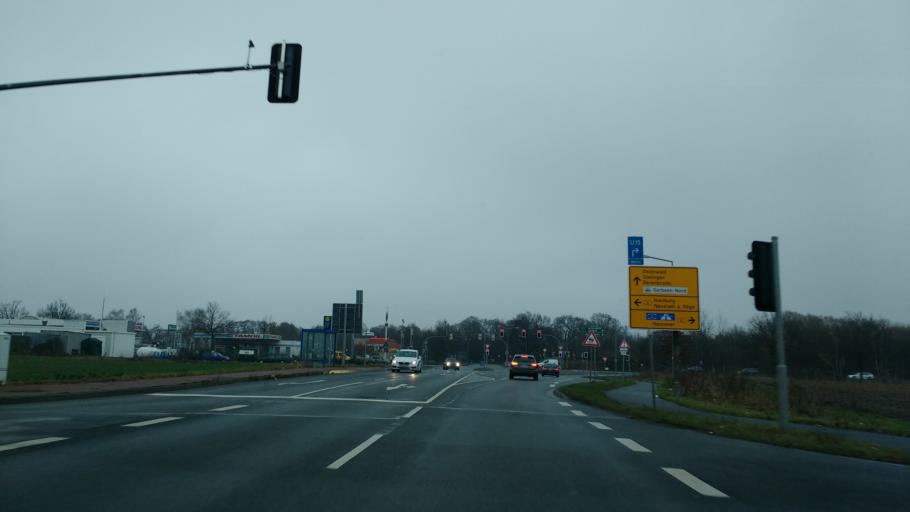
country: DE
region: Lower Saxony
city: Garbsen-Mitte
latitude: 52.4380
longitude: 9.5885
